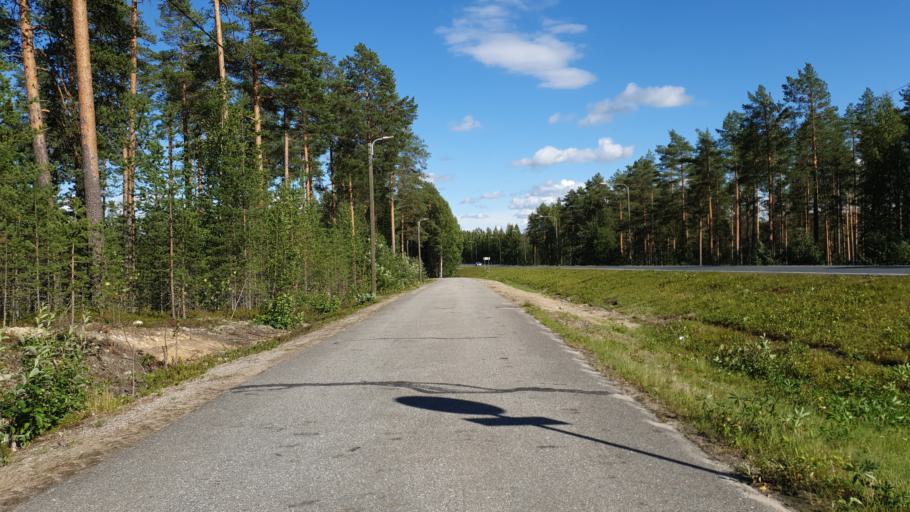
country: FI
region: Kainuu
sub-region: Kehys-Kainuu
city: Kuhmo
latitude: 64.0926
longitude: 29.4463
